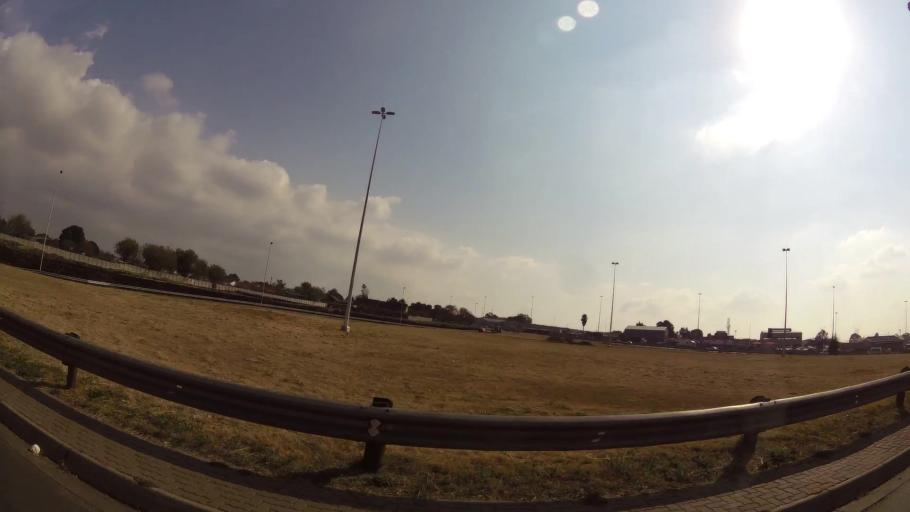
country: ZA
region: Gauteng
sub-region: Ekurhuleni Metropolitan Municipality
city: Germiston
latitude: -26.1764
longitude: 28.1972
